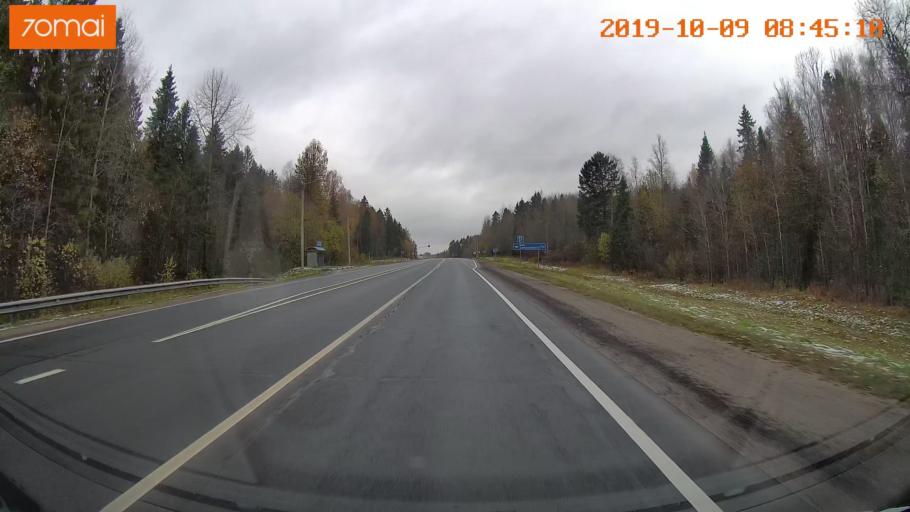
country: RU
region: Vologda
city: Gryazovets
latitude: 59.0453
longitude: 40.0966
